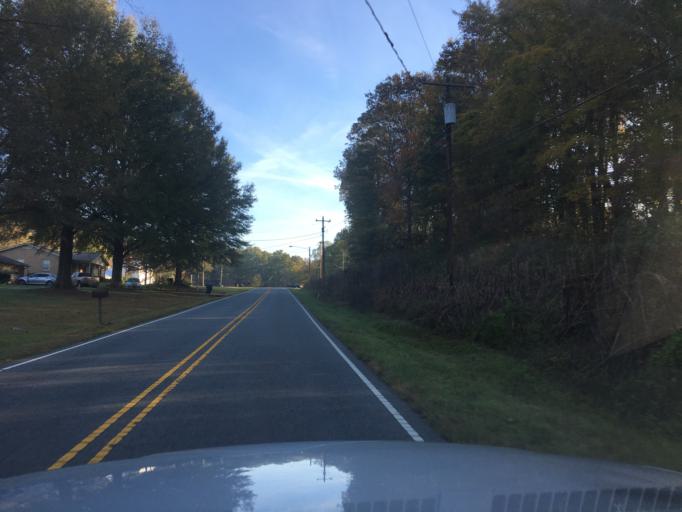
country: US
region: North Carolina
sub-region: Catawba County
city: Newton
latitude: 35.6656
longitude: -81.2507
